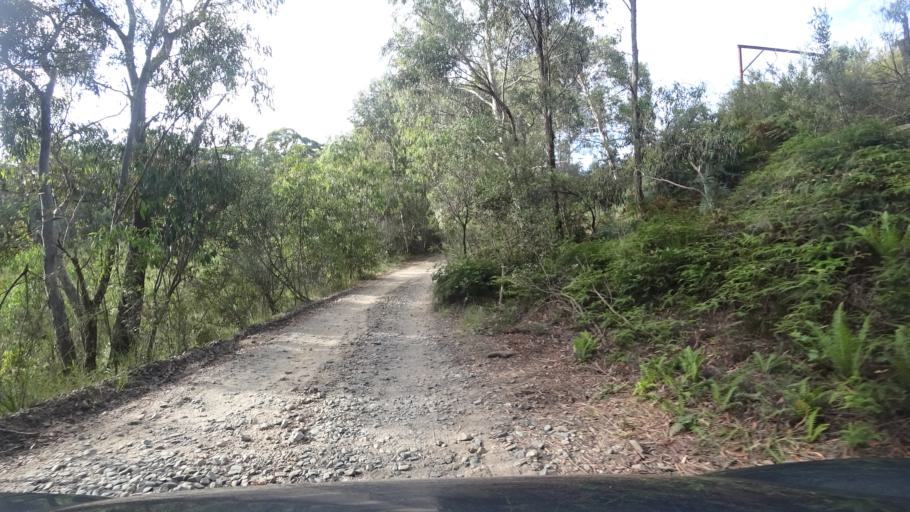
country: AU
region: New South Wales
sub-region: Lithgow
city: Lithgow
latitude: -33.4822
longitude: 150.2460
